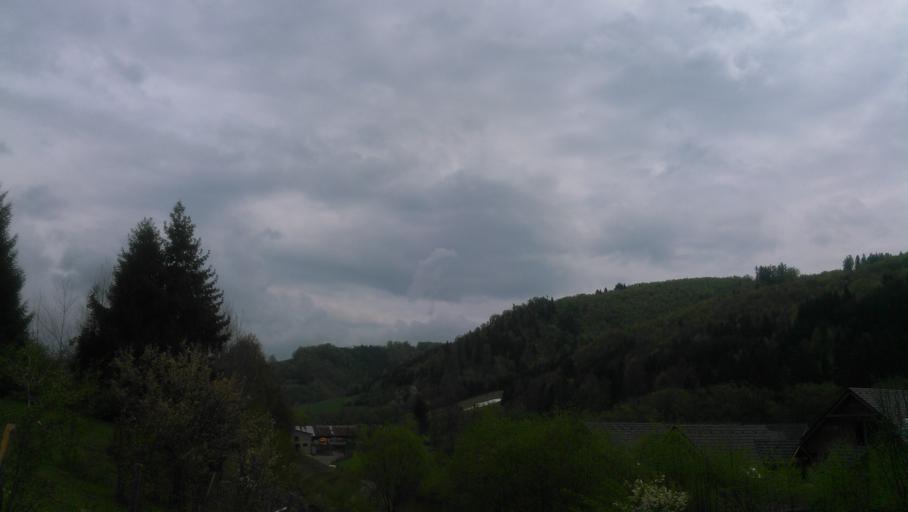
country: SK
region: Banskobystricky
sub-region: Okres Banska Bystrica
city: Brezno
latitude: 48.8459
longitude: 19.6114
